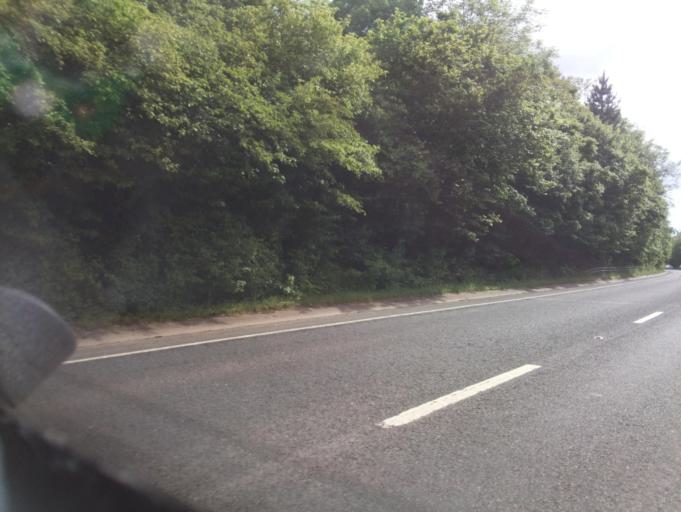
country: GB
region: England
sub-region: Worcestershire
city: Bransford
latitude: 52.1866
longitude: -2.2714
